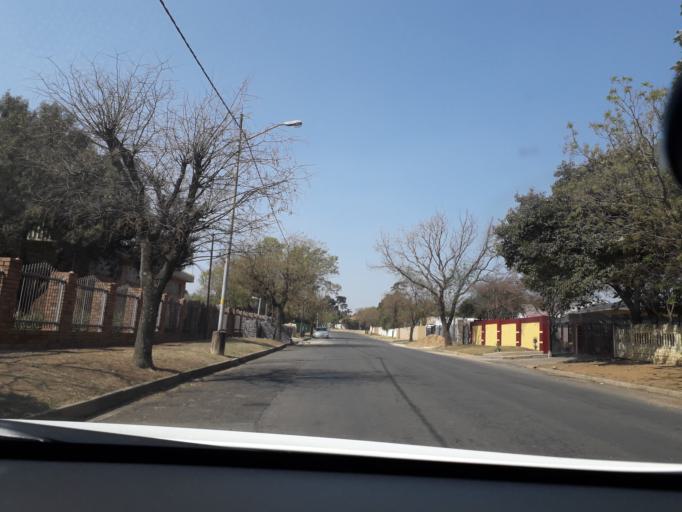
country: ZA
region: Gauteng
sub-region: City of Johannesburg Metropolitan Municipality
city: Modderfontein
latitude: -26.0933
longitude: 28.2279
